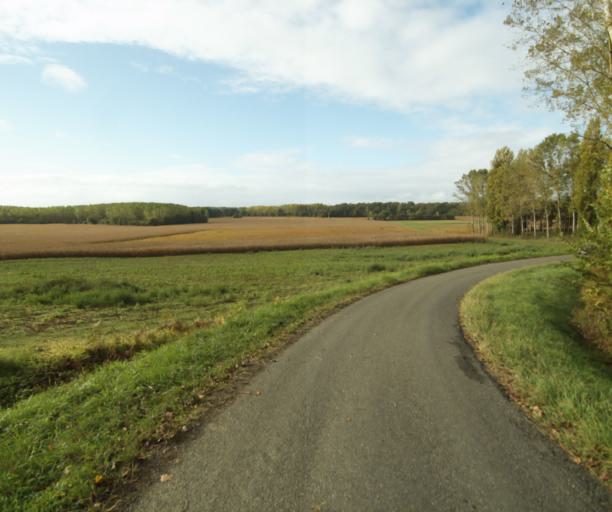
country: FR
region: Midi-Pyrenees
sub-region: Departement du Gers
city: Nogaro
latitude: 43.8102
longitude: -0.0635
